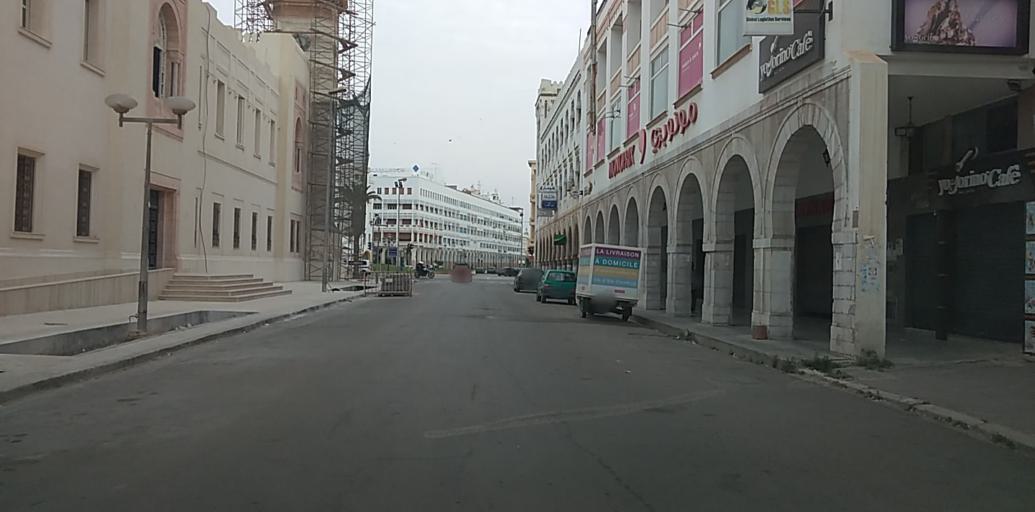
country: TN
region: Safaqis
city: Sfax
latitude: 34.7321
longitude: 10.7645
